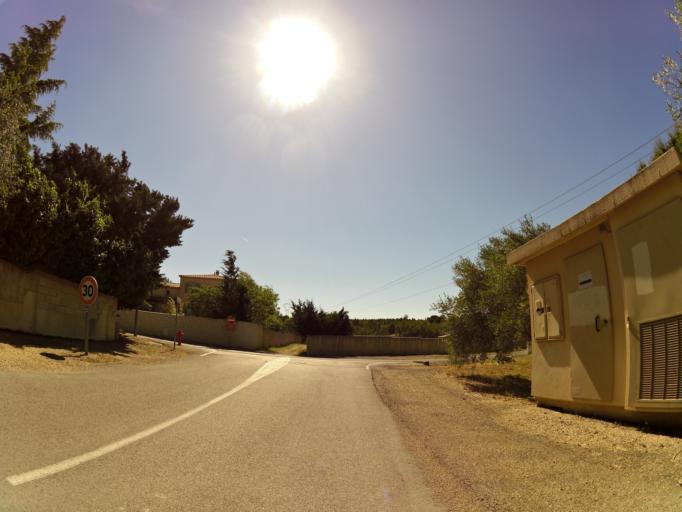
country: FR
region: Languedoc-Roussillon
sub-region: Departement de l'Herault
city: Villetelle
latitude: 43.7344
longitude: 4.1344
